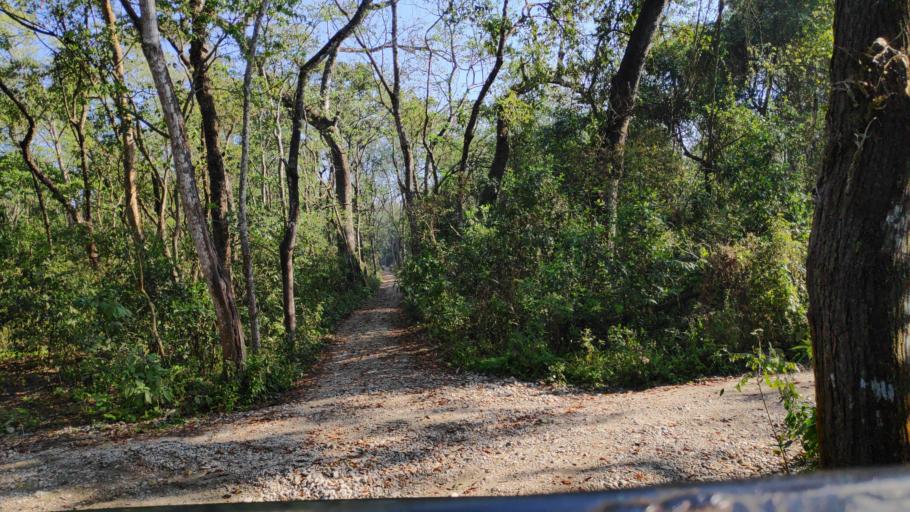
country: NP
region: Central Region
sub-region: Narayani Zone
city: Bharatpur
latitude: 27.5619
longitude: 84.5373
